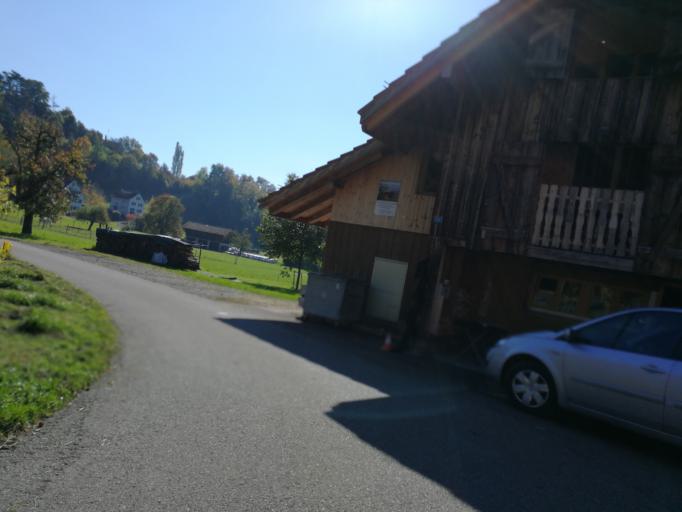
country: CH
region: Zurich
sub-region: Bezirk Meilen
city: Maennedorf / Ausserfeld
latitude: 47.2477
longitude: 8.7121
